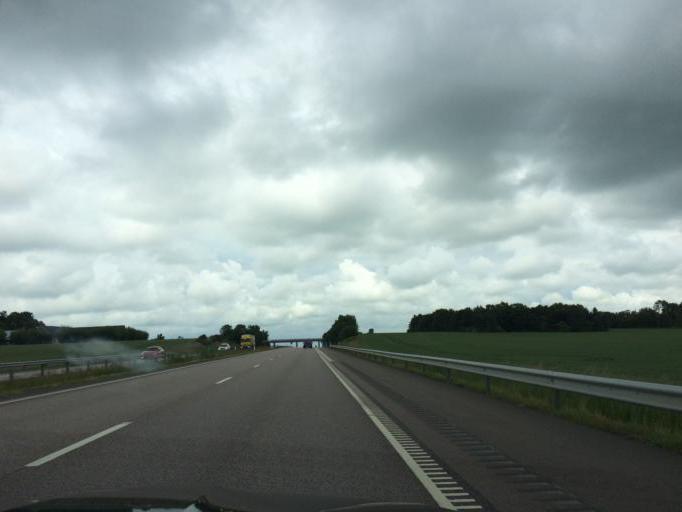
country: SE
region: Skane
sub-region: Helsingborg
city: Hyllinge
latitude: 56.1011
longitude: 12.7978
